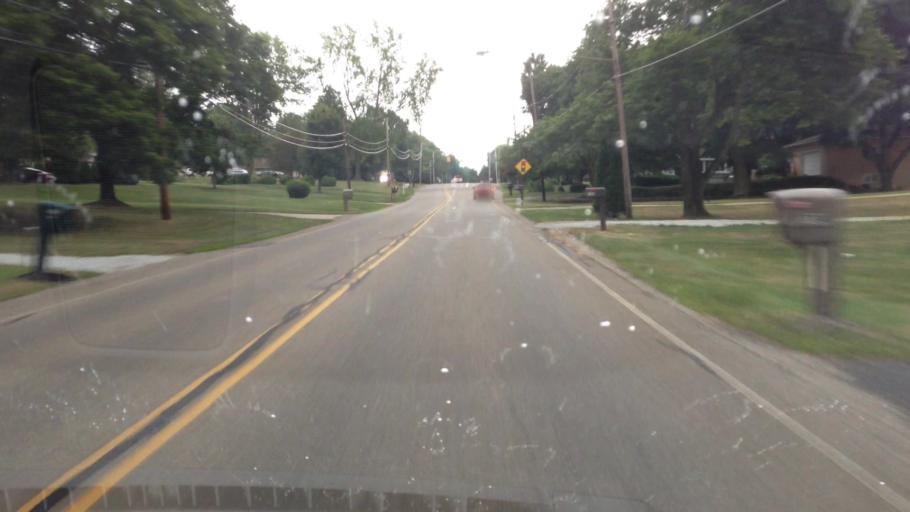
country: US
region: Ohio
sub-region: Summit County
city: Barberton
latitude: 41.0121
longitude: -81.5716
